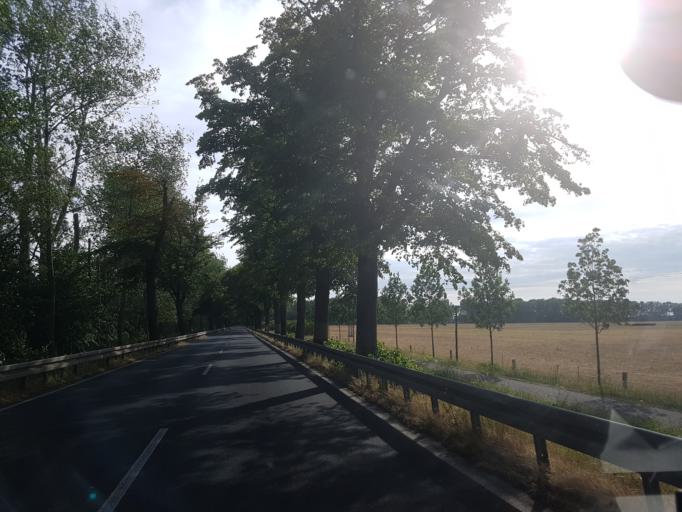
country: DE
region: Brandenburg
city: Herzberg
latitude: 51.7153
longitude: 13.2790
